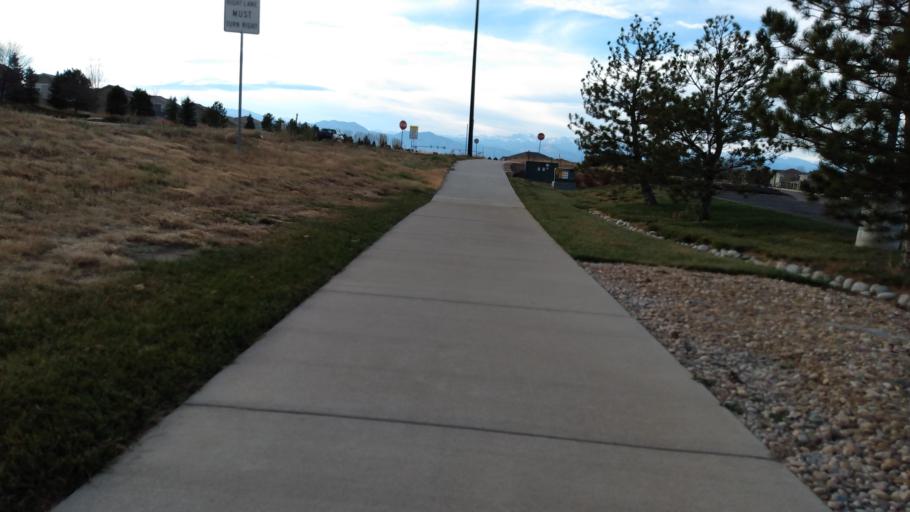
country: US
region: Colorado
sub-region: Boulder County
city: Erie
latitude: 40.0005
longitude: -105.0220
